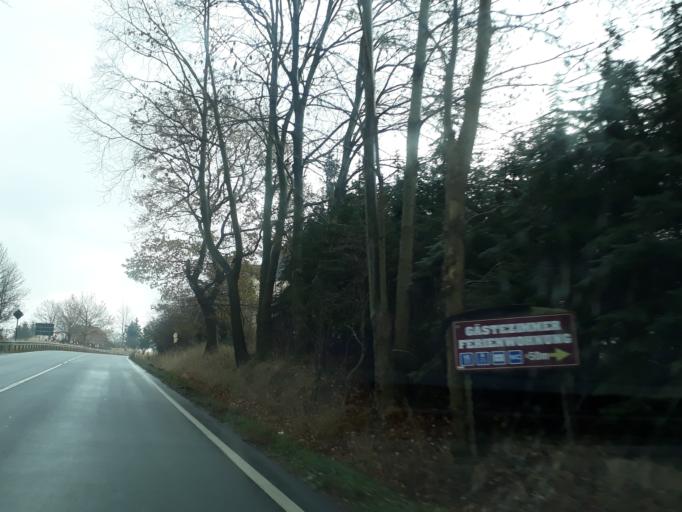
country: DE
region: Saxony
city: Lobau
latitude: 51.1188
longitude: 14.6418
